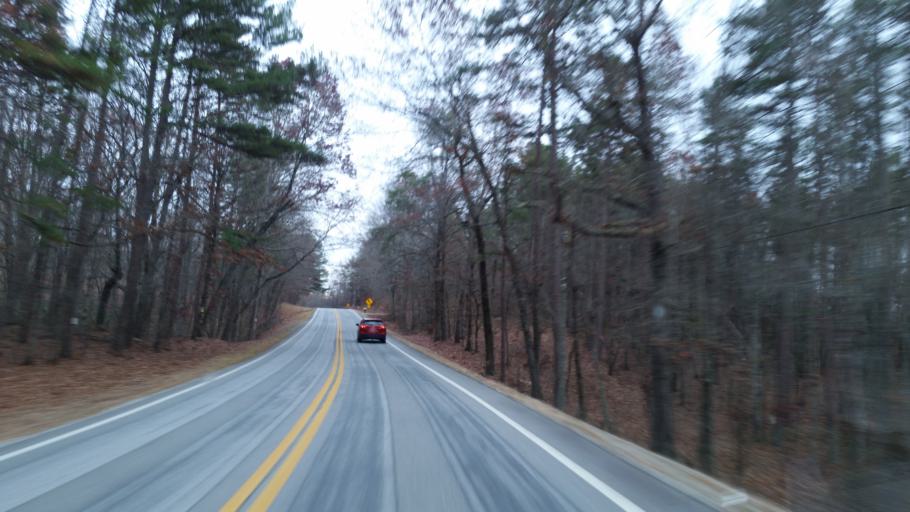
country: US
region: Georgia
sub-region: Dawson County
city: Dawsonville
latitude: 34.4264
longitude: -84.0527
